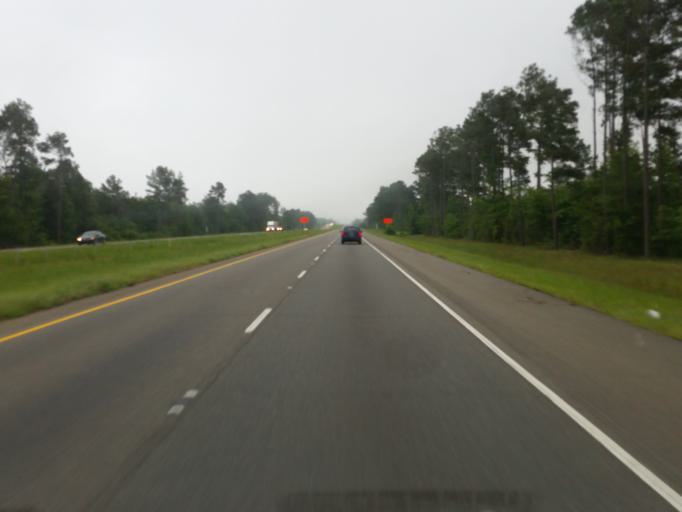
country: US
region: Louisiana
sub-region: Bossier Parish
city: Haughton
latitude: 32.5815
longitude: -93.4033
